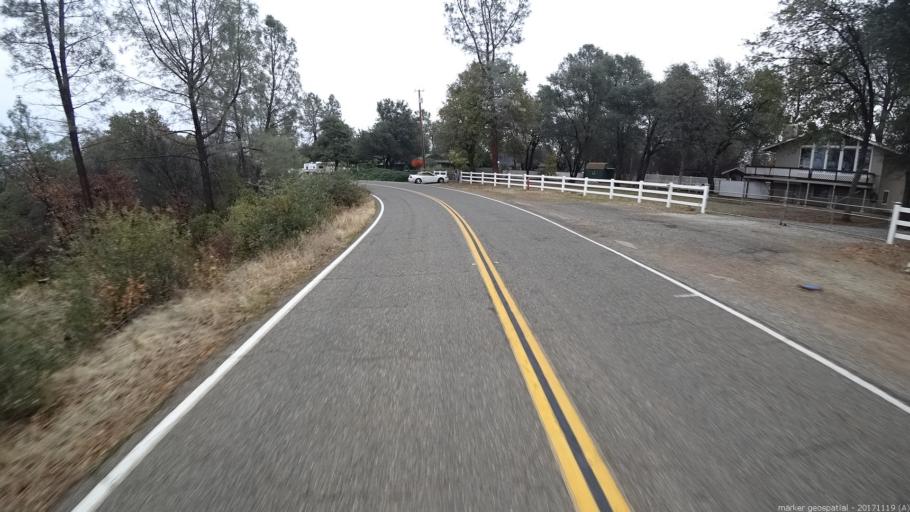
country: US
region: California
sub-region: Shasta County
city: Redding
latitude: 40.4868
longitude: -122.4463
